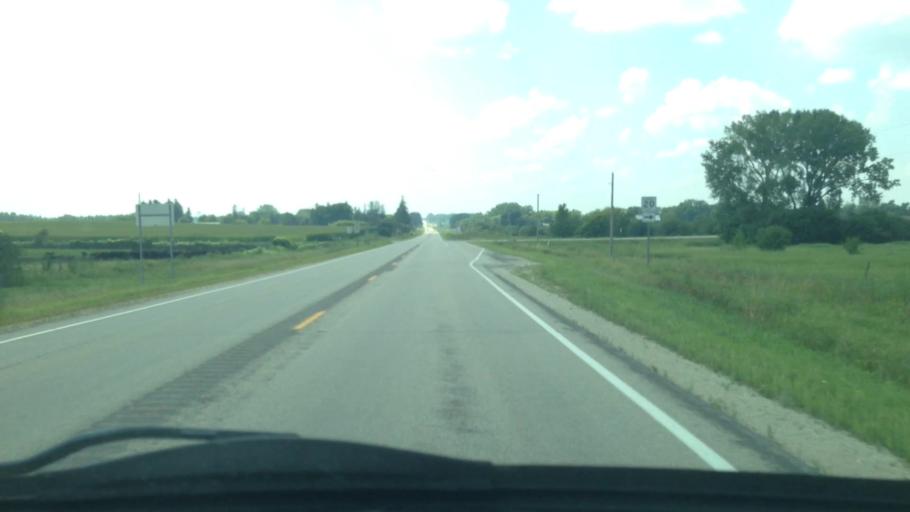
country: US
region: Minnesota
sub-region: Olmsted County
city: Stewartville
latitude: 43.8555
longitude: -92.4360
